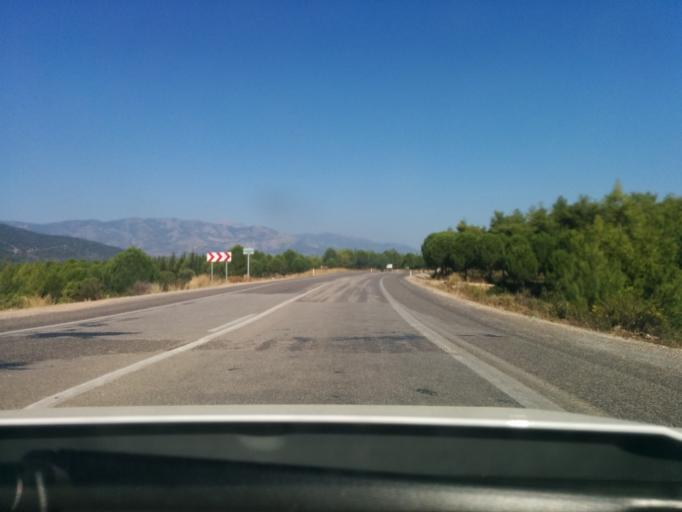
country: TR
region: Mugla
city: Esen
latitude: 36.3731
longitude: 29.3233
